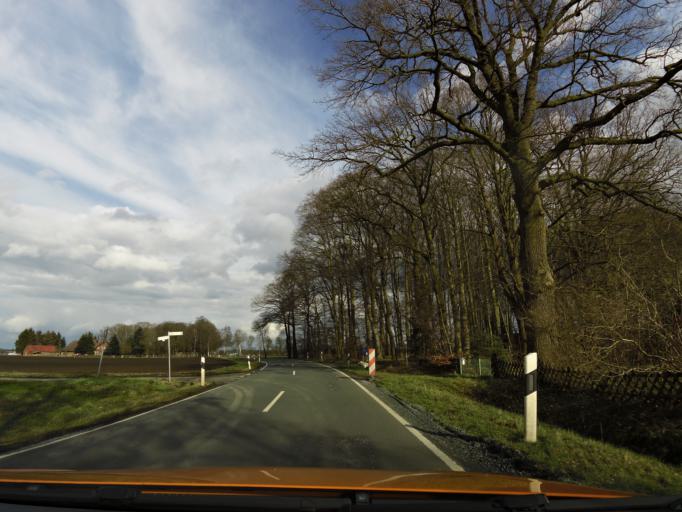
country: DE
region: Lower Saxony
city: Dunsen
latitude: 52.8874
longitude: 8.6376
